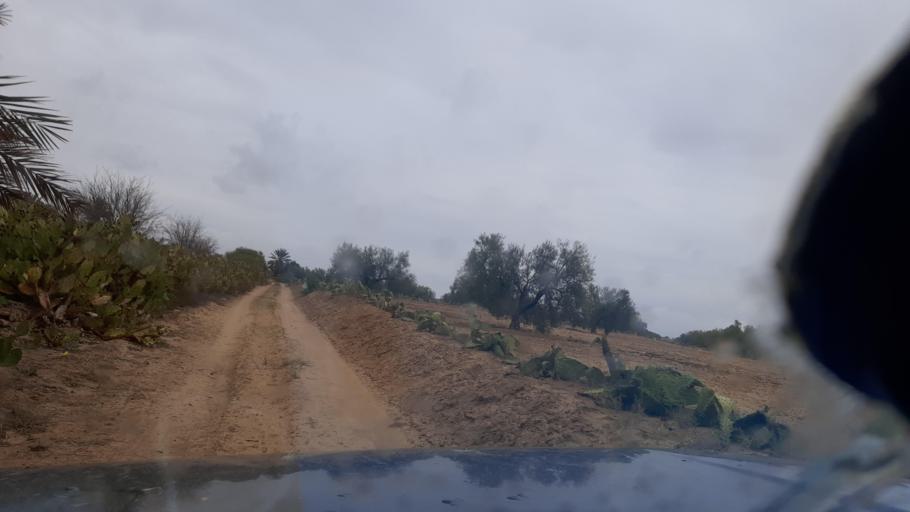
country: TN
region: Al Mahdiyah
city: Shurban
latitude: 35.4357
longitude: 10.4070
